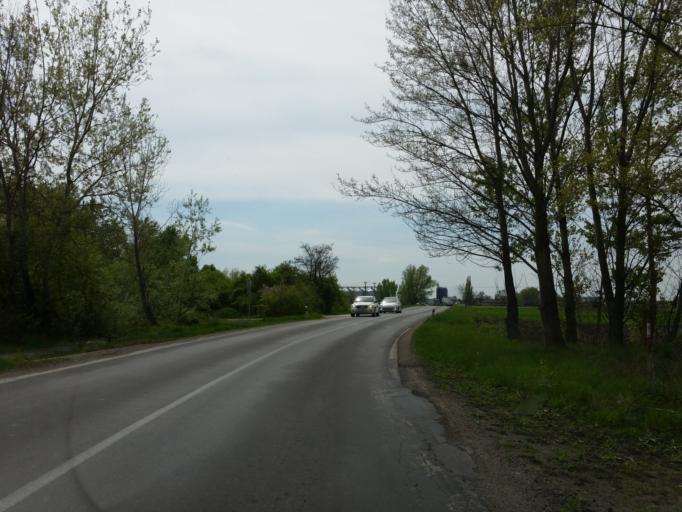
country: SK
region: Trnavsky
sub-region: Okres Dunajska Streda
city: Velky Meder
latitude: 47.8712
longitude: 17.7912
